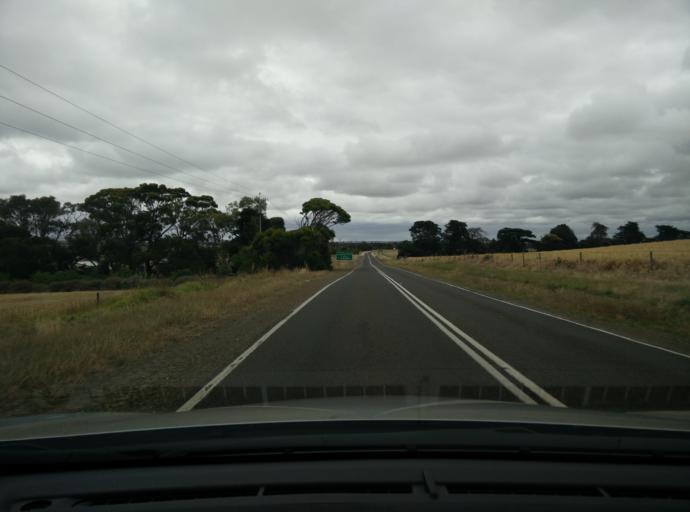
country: AU
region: South Australia
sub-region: Kangaroo Island
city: Kingscote
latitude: -35.6710
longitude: 137.5926
